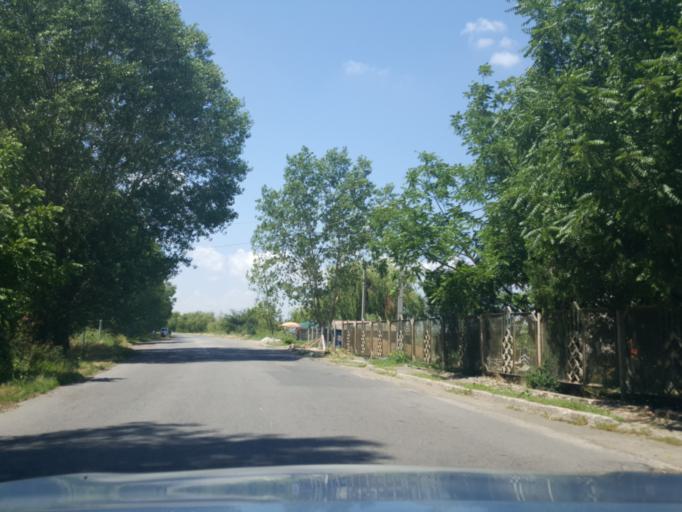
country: UA
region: Odessa
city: Bilyayivka
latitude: 46.4123
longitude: 30.1212
